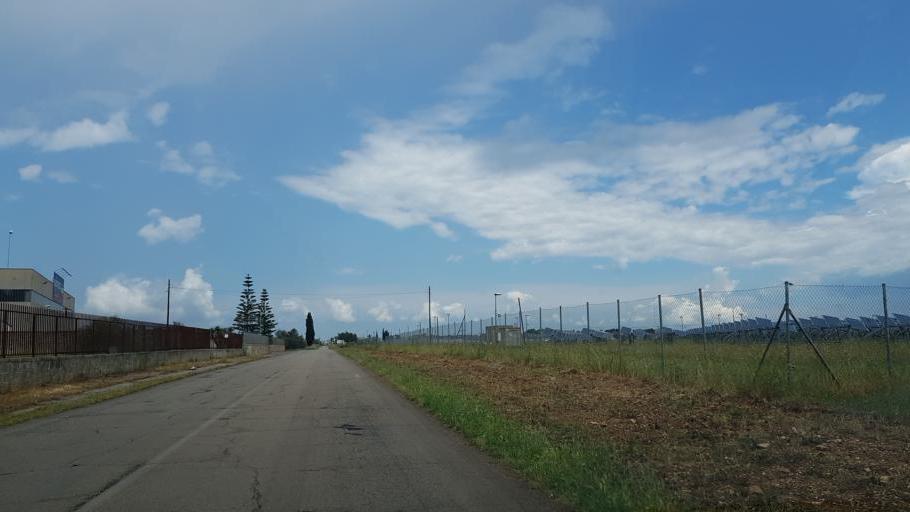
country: IT
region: Apulia
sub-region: Provincia di Brindisi
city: San Donaci
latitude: 40.4410
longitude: 17.9043
